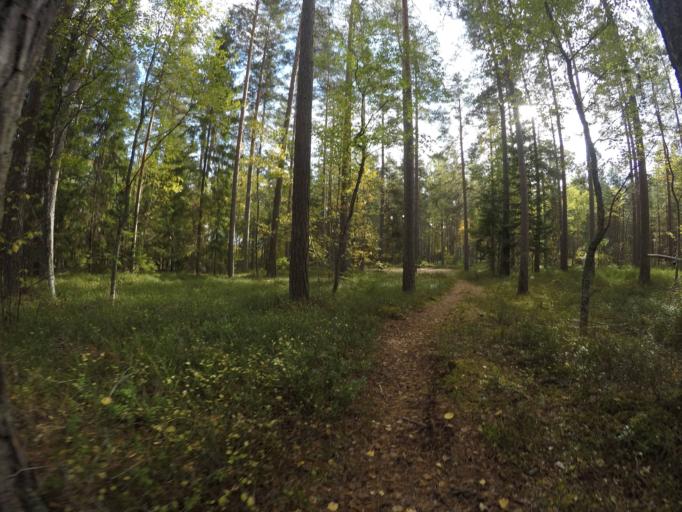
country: SE
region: Vaestmanland
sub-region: Kungsors Kommun
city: Kungsoer
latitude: 59.3183
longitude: 16.1146
